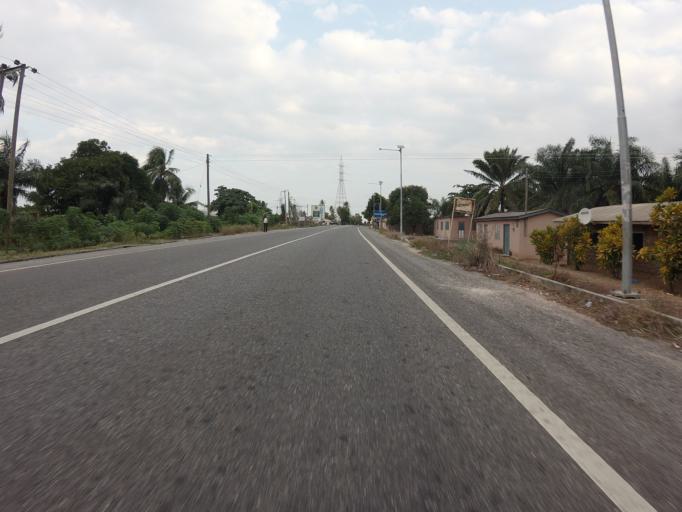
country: GH
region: Volta
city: Ho
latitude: 6.2616
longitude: 0.5484
